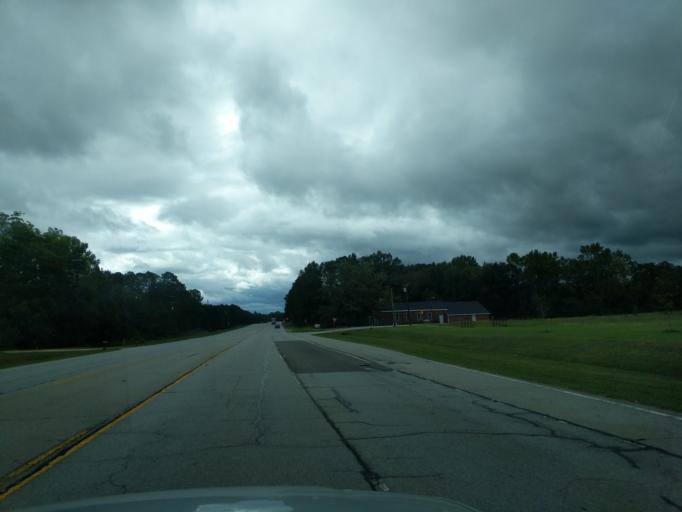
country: US
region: Georgia
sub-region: Wilkes County
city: Washington
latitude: 33.7069
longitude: -82.6961
